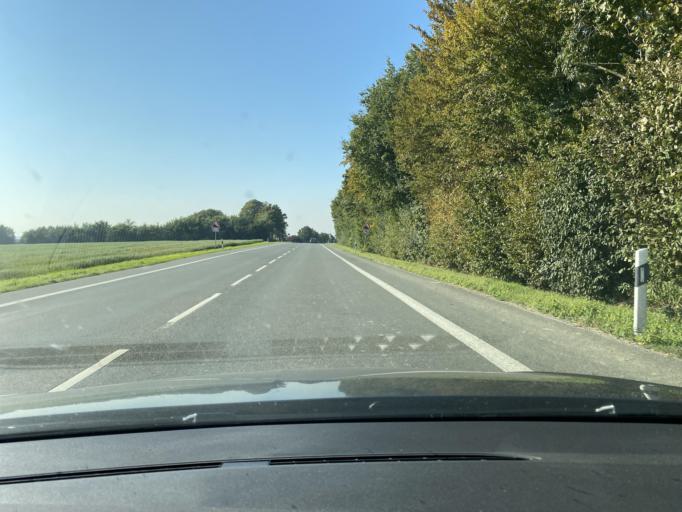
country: DE
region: North Rhine-Westphalia
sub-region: Regierungsbezirk Munster
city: Schoppingen
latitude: 52.0895
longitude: 7.2651
